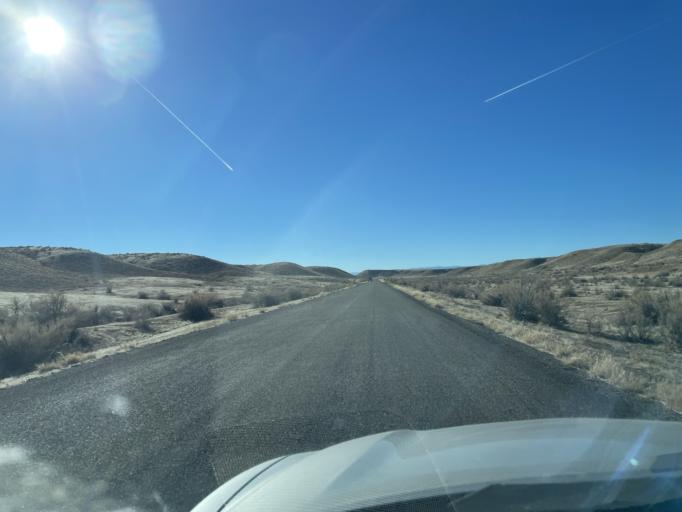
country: US
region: Colorado
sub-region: Mesa County
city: Loma
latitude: 39.2059
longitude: -109.0982
